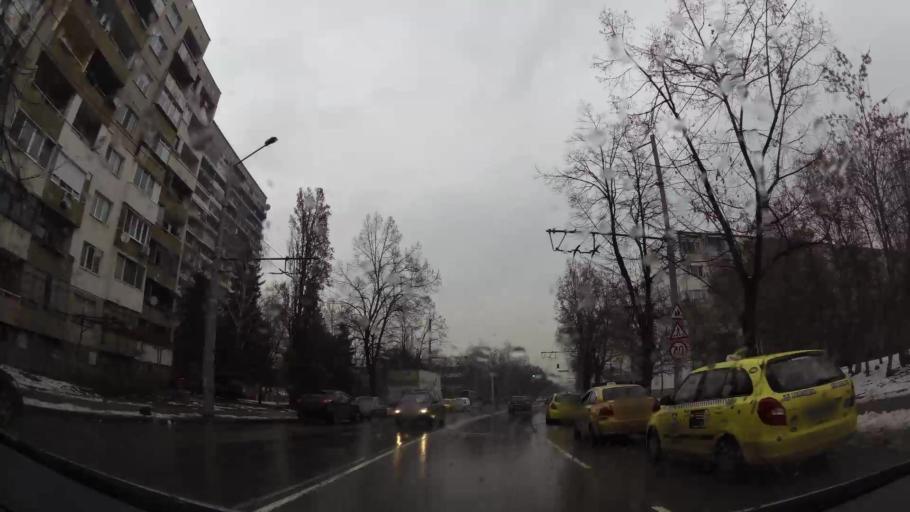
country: BG
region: Sofia-Capital
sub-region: Stolichna Obshtina
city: Sofia
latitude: 42.6635
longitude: 23.2965
